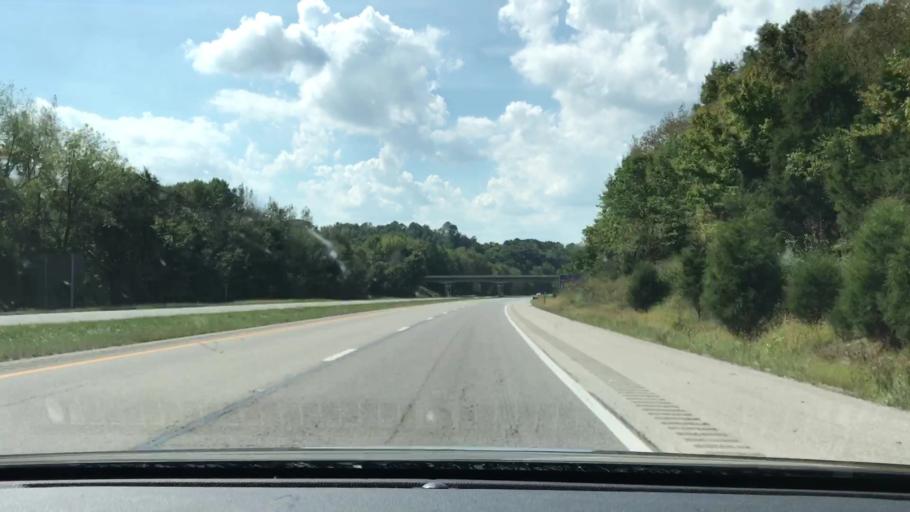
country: US
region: Kentucky
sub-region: Barren County
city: Glasgow
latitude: 36.9747
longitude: -85.9075
